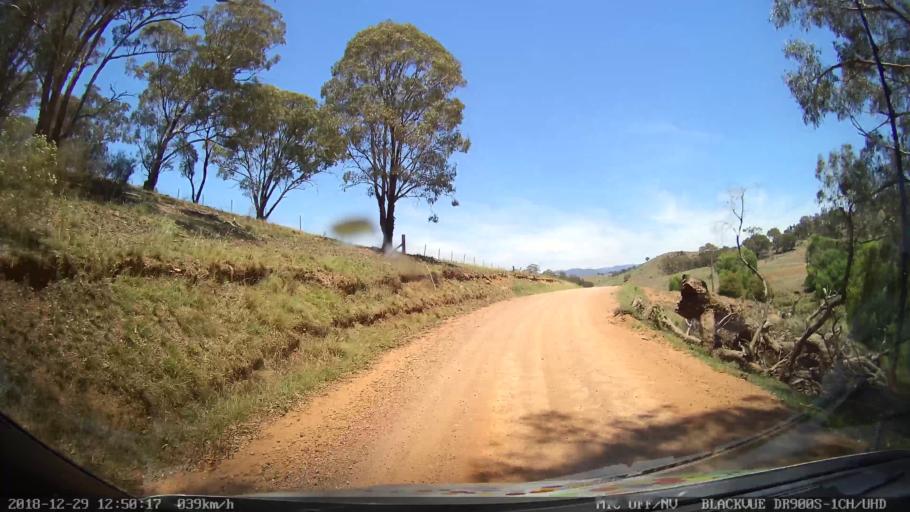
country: AU
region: Australian Capital Territory
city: Macarthur
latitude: -35.6695
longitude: 149.2036
